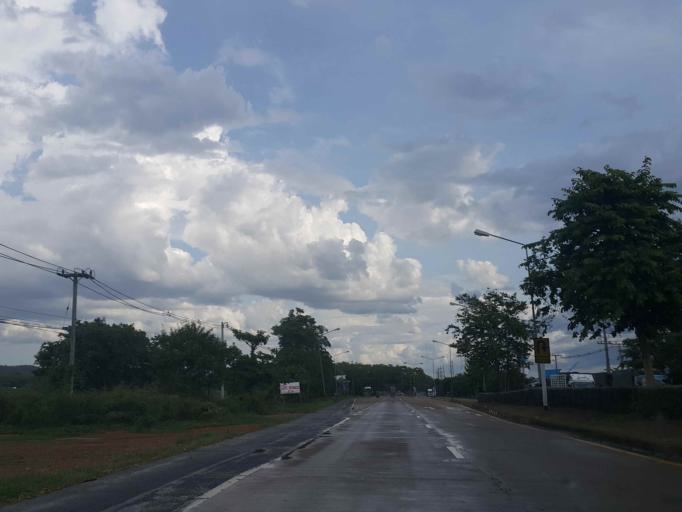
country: TH
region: Phrae
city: Den Chai
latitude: 17.9948
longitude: 100.0993
